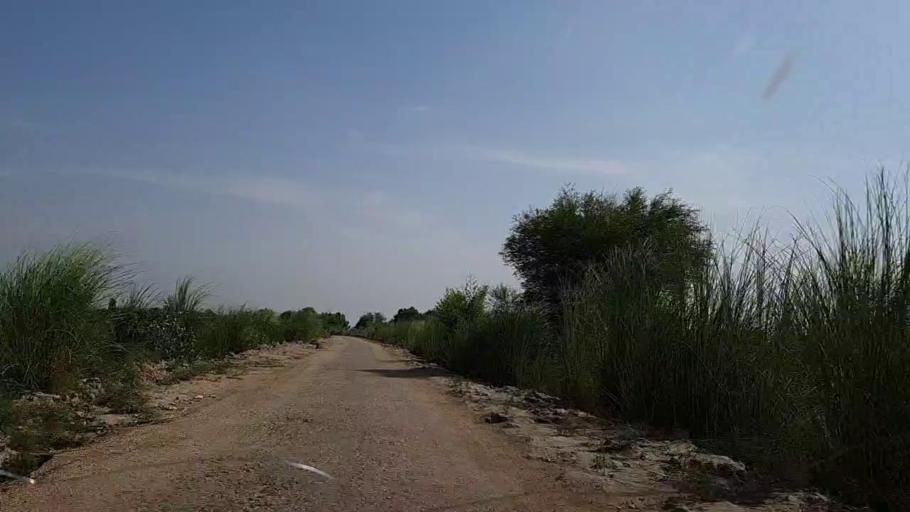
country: PK
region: Sindh
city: Khanpur
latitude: 27.7138
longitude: 69.3622
